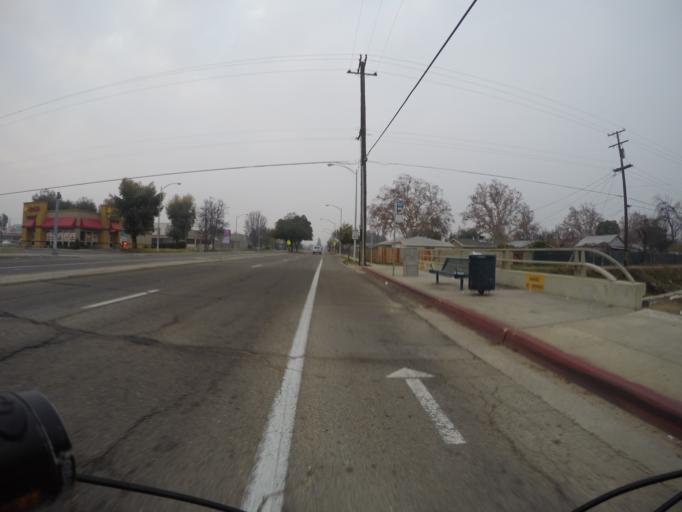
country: US
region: California
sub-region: Fresno County
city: Fresno
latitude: 36.7649
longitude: -119.7726
